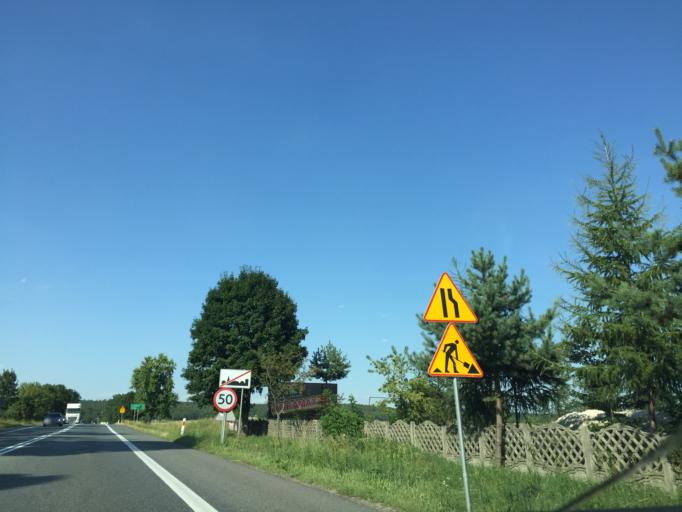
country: PL
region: Swietokrzyskie
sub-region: Powiat jedrzejowski
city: Wodzislaw
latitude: 50.4495
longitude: 20.1444
